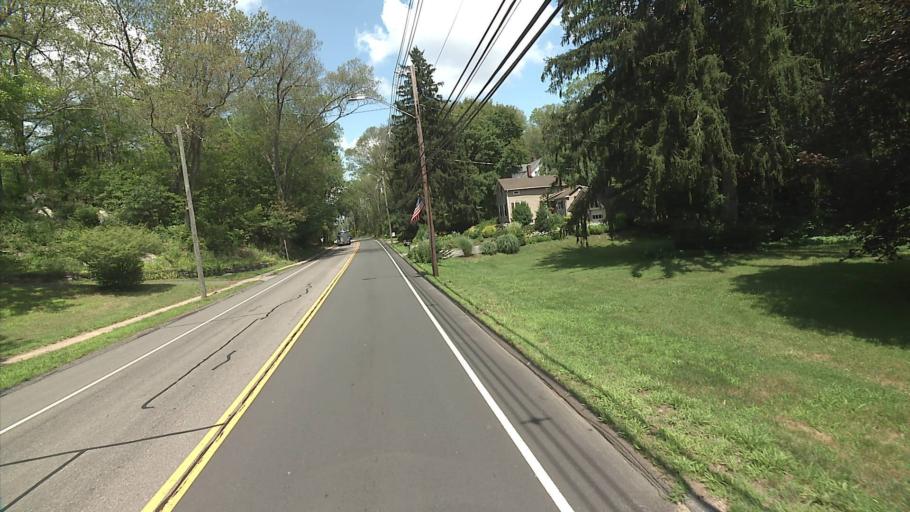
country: US
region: Connecticut
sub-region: Middlesex County
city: Deep River Center
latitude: 41.3766
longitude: -72.4319
